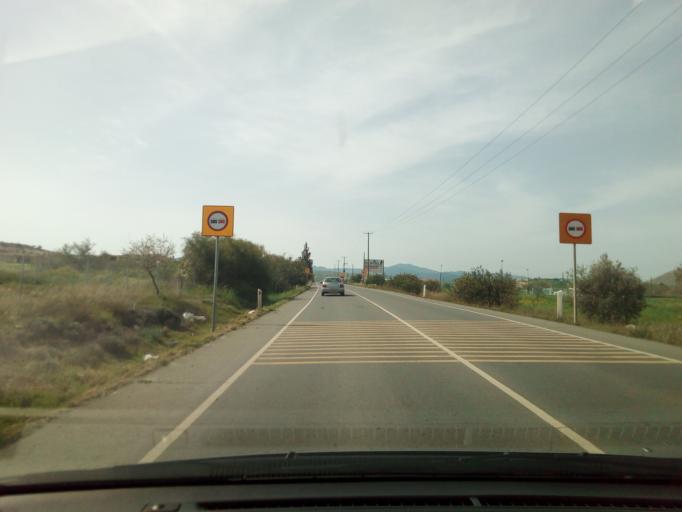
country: CY
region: Lefkosia
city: Arediou
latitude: 35.0507
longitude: 33.1886
